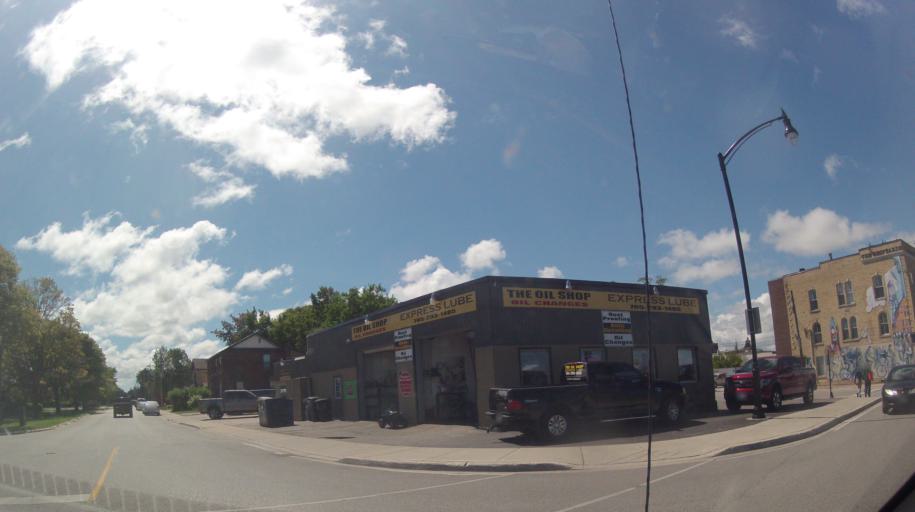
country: CA
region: Ontario
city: Collingwood
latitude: 44.5032
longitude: -80.2154
